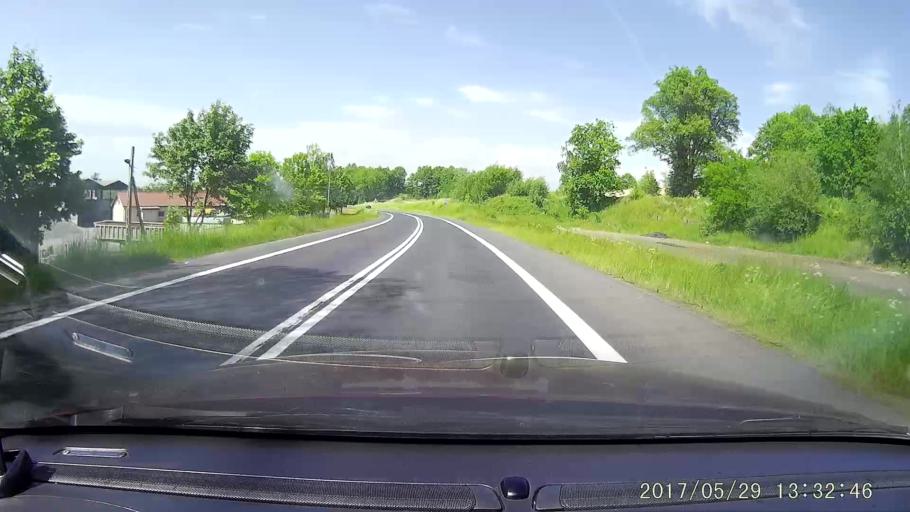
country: PL
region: Lower Silesian Voivodeship
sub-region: Powiat lubanski
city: Luban
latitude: 51.0891
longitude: 15.3224
